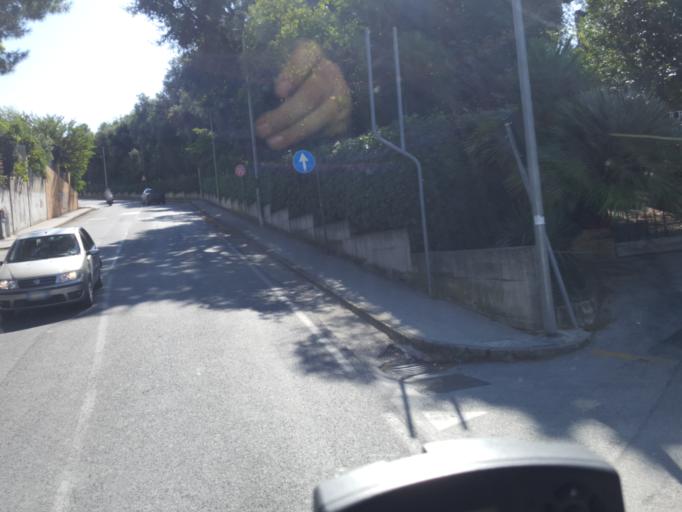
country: IT
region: The Marches
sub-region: Provincia di Ancona
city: Le Grazie di Ancona
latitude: 43.6034
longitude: 13.5091
